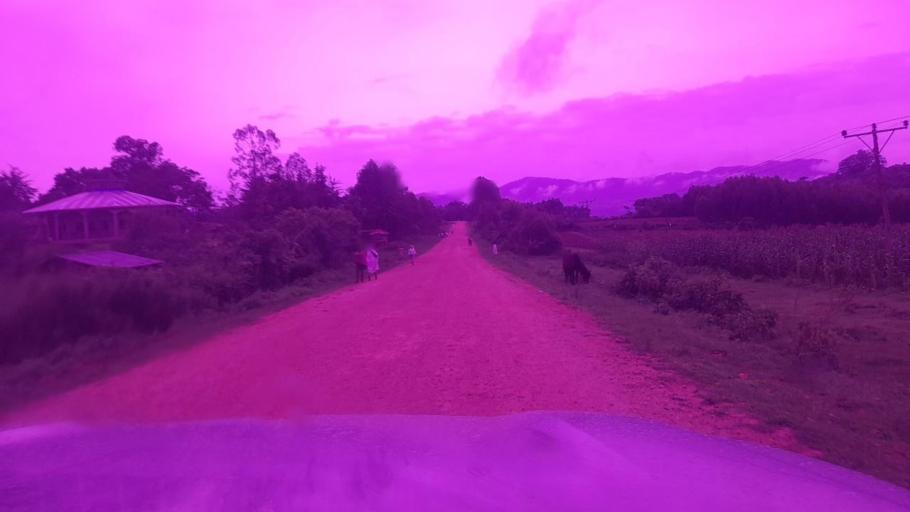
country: ET
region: Southern Nations, Nationalities, and People's Region
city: Bonga
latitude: 7.4406
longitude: 36.1600
